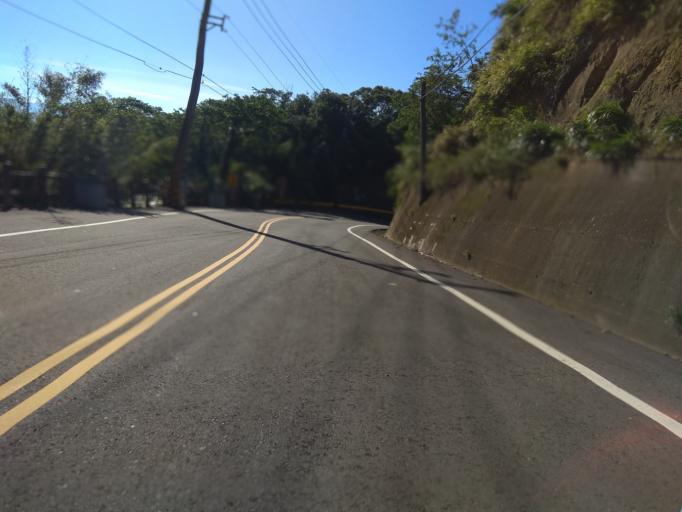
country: TW
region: Taiwan
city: Daxi
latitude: 24.8619
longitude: 121.1548
